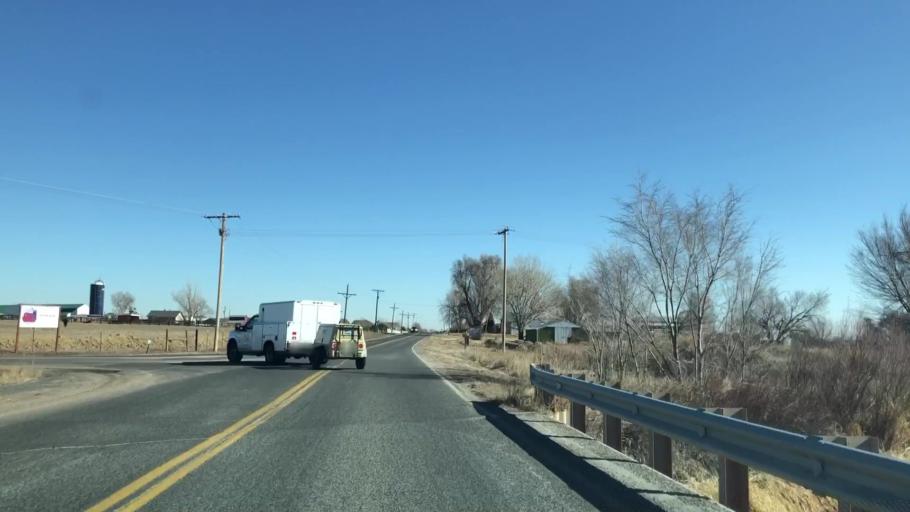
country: US
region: Colorado
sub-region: Weld County
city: Windsor
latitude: 40.4865
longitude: -104.9406
